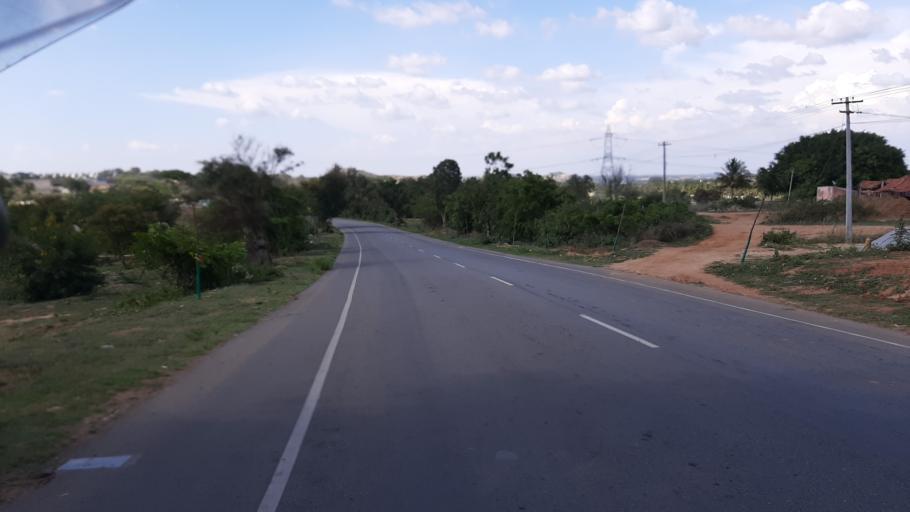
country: IN
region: Tamil Nadu
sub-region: Krishnagiri
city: Denkanikota
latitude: 12.5401
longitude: 77.7889
